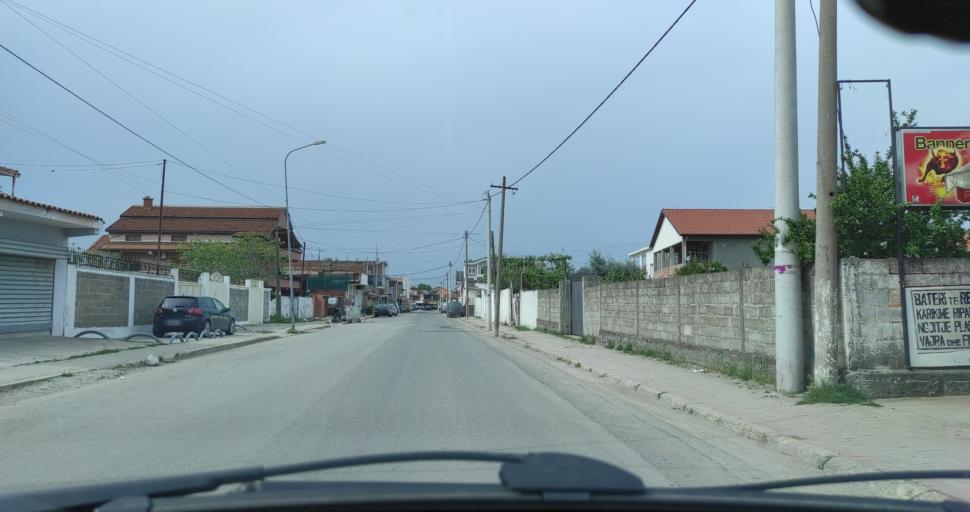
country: AL
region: Durres
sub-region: Rrethi i Krujes
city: Fushe-Kruje
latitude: 41.4762
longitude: 19.7180
